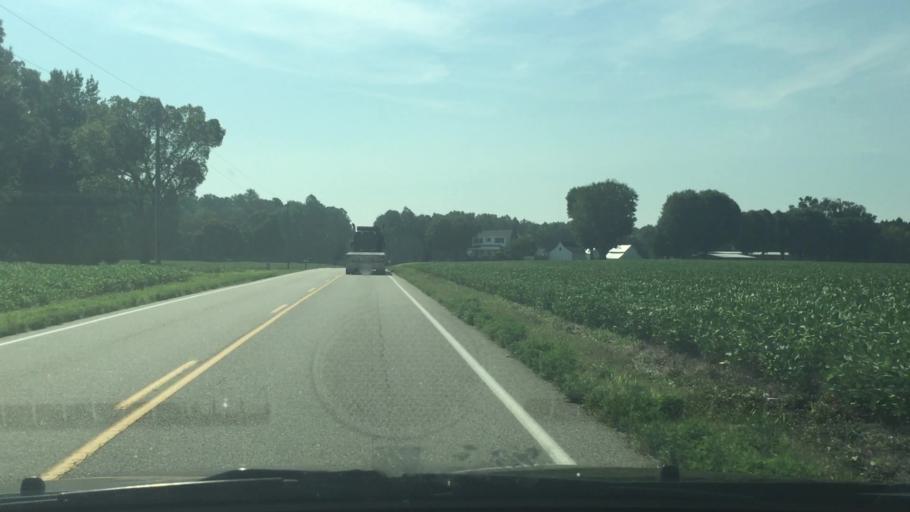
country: US
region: Virginia
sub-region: Prince George County
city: Prince George
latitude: 37.0746
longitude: -77.3480
